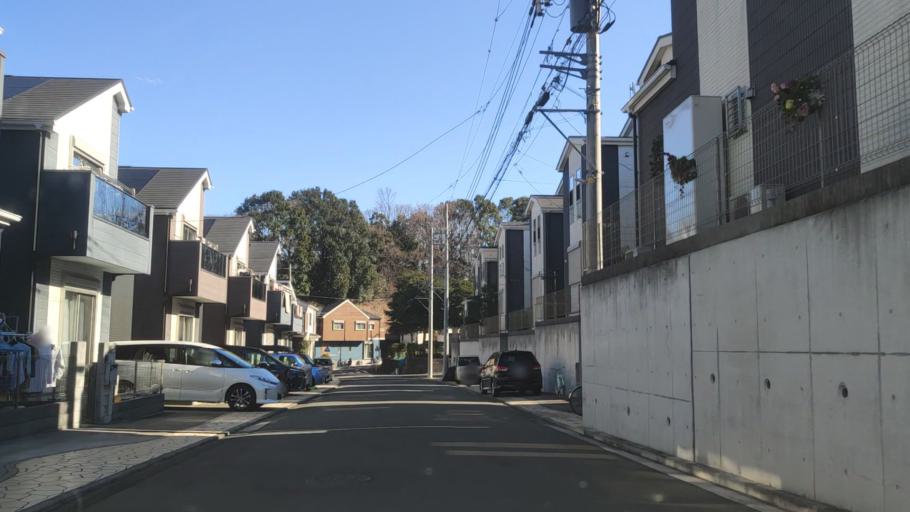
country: JP
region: Kanagawa
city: Minami-rinkan
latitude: 35.5059
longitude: 139.5265
